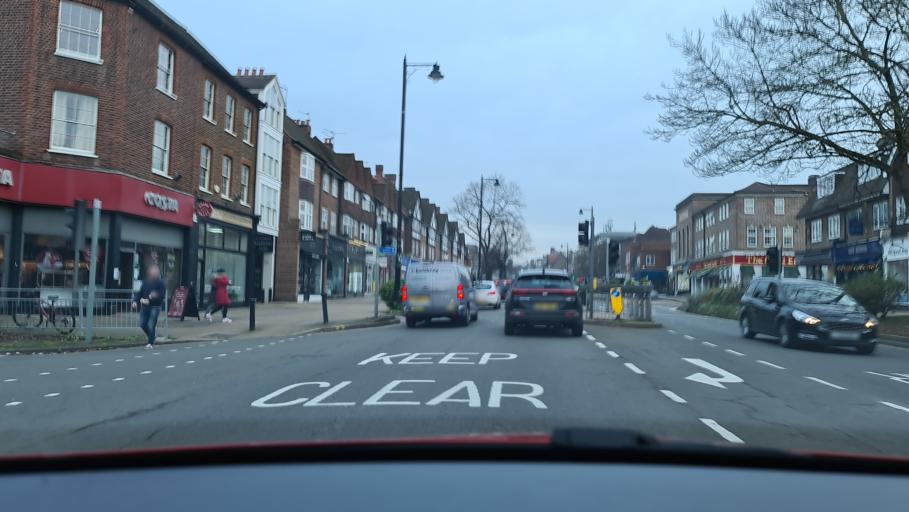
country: GB
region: England
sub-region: Surrey
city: Esher
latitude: 51.3711
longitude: -0.3628
